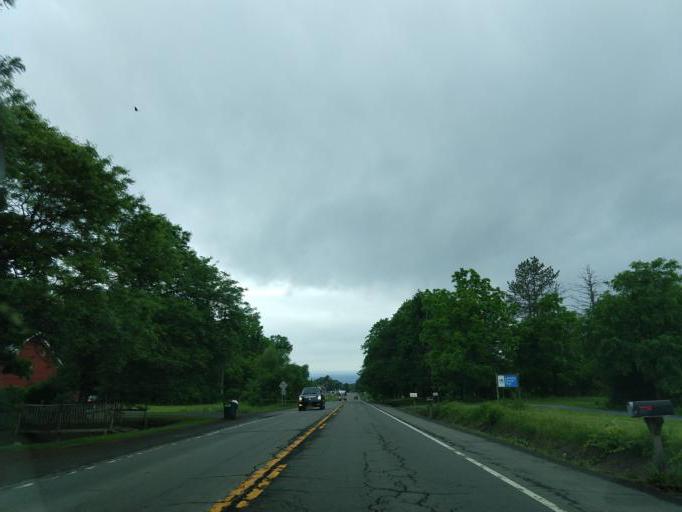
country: US
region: New York
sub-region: Tompkins County
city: Lansing
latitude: 42.5383
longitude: -76.4971
